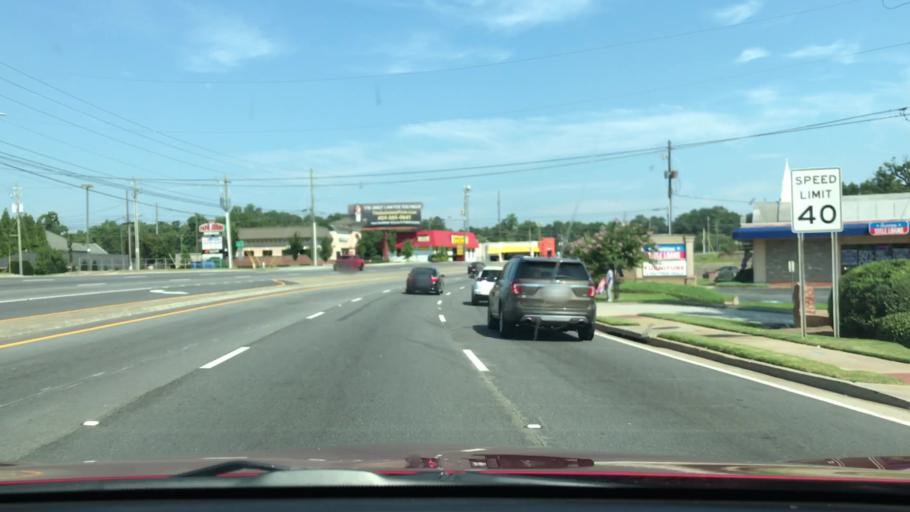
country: US
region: Georgia
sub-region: Gwinnett County
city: Norcross
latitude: 33.8996
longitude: -84.2037
